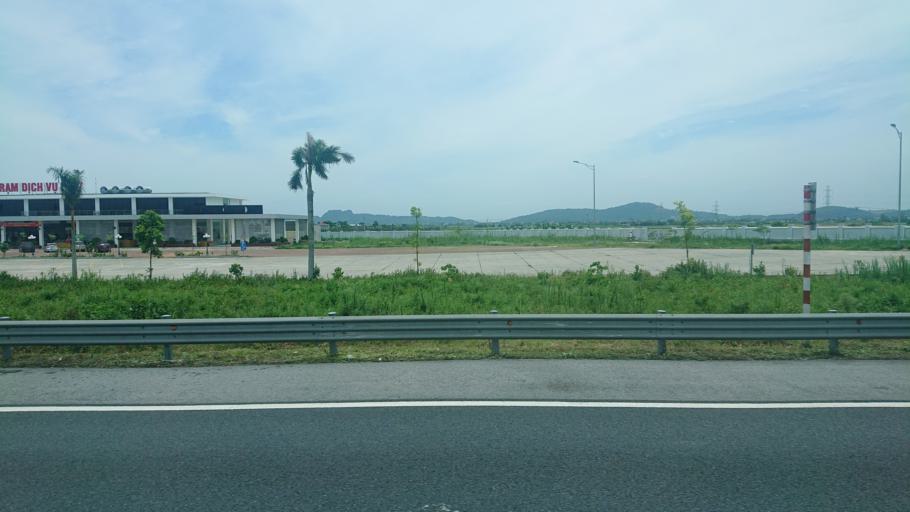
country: VN
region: Hai Phong
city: An Lao
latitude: 20.7930
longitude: 106.5489
